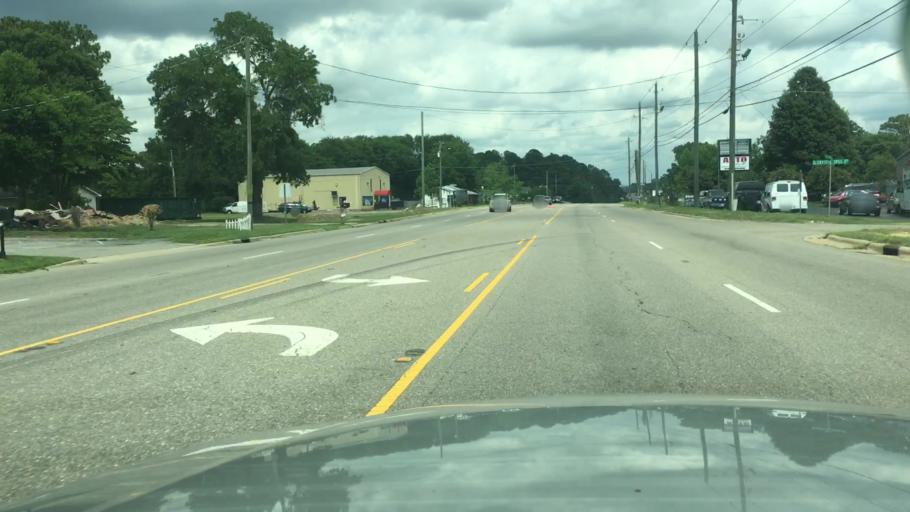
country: US
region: North Carolina
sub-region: Cumberland County
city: Hope Mills
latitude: 35.0092
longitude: -78.9573
